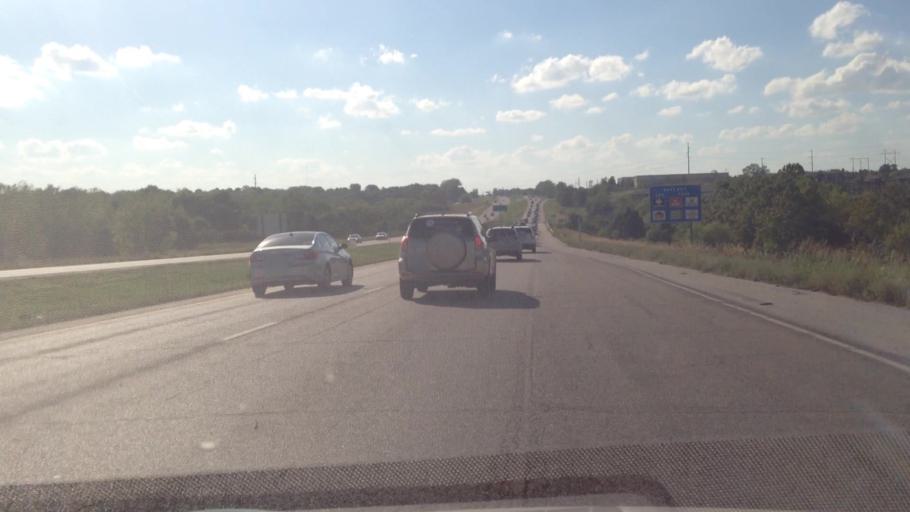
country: US
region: Kansas
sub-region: Johnson County
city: Olathe
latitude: 38.9421
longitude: -94.8035
